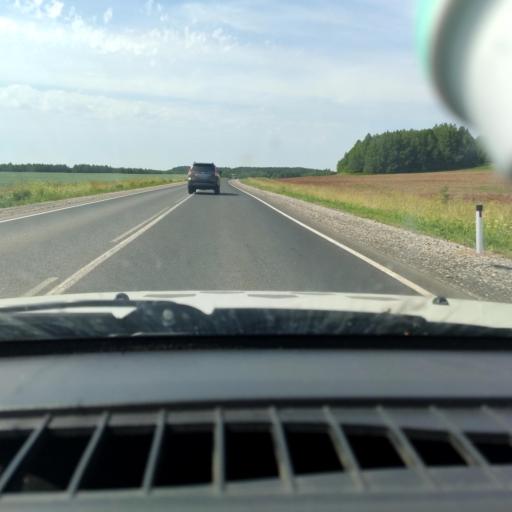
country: RU
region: Perm
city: Siva
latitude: 58.4015
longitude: 54.4913
